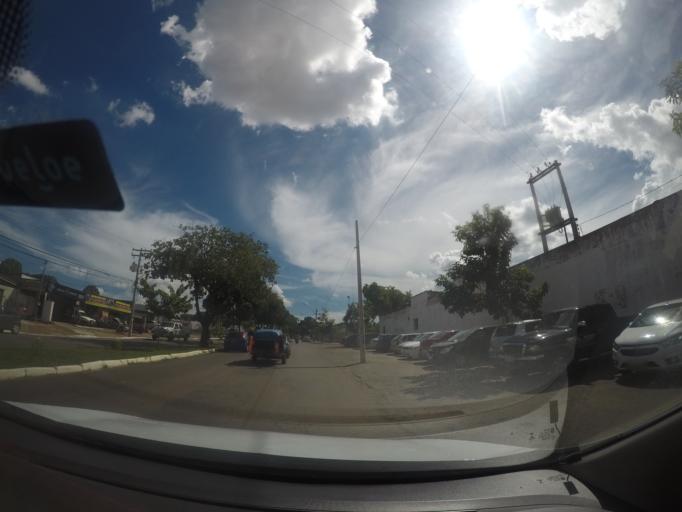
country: BR
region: Goias
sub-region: Goiania
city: Goiania
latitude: -16.6786
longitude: -49.2974
